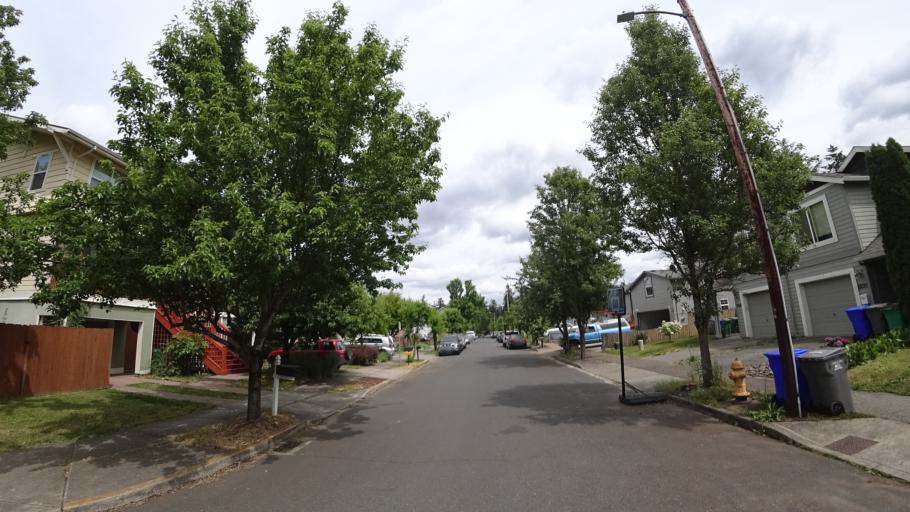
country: US
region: Oregon
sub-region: Multnomah County
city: Lents
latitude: 45.4875
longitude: -122.5398
